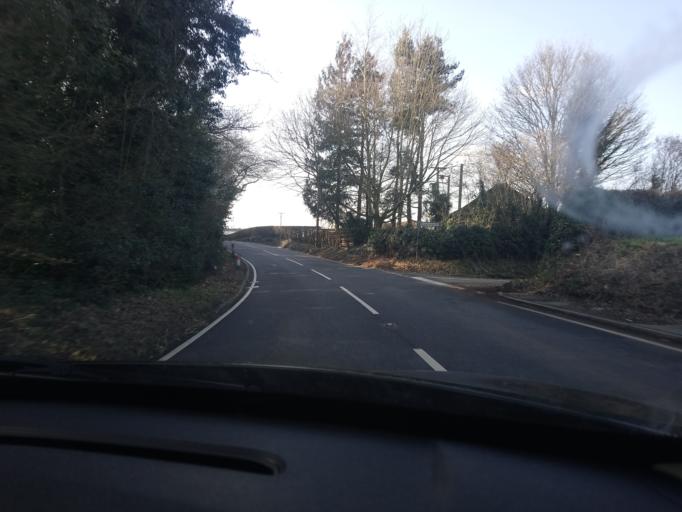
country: GB
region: England
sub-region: Shropshire
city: Clive
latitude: 52.8000
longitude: -2.7619
